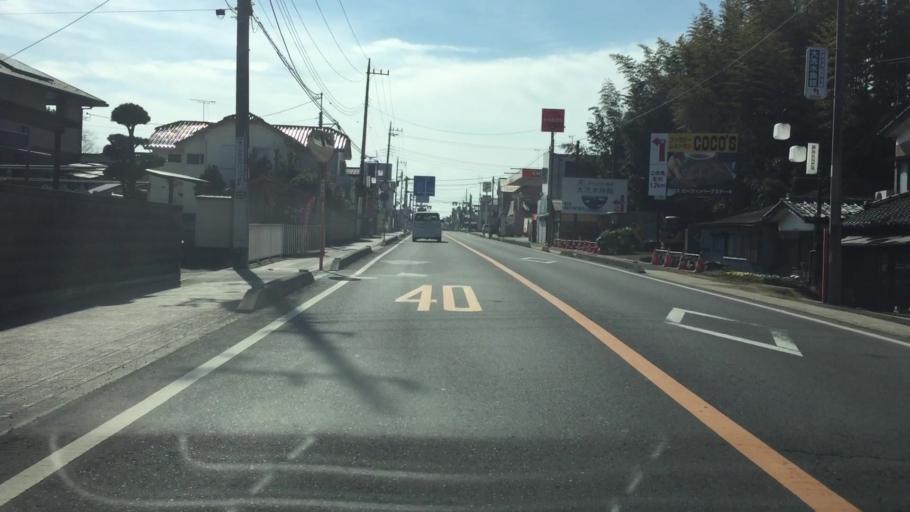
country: JP
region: Ibaraki
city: Oarai
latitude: 36.3195
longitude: 140.5648
